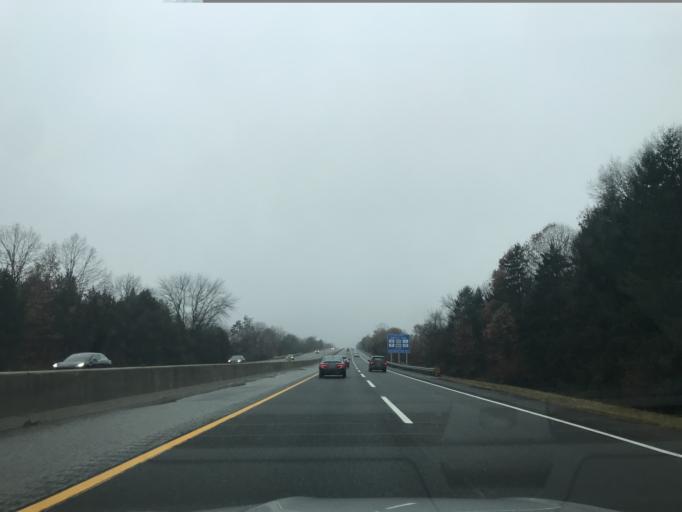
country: US
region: New Jersey
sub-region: Gloucester County
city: Swedesboro
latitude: 39.7317
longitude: -75.3127
